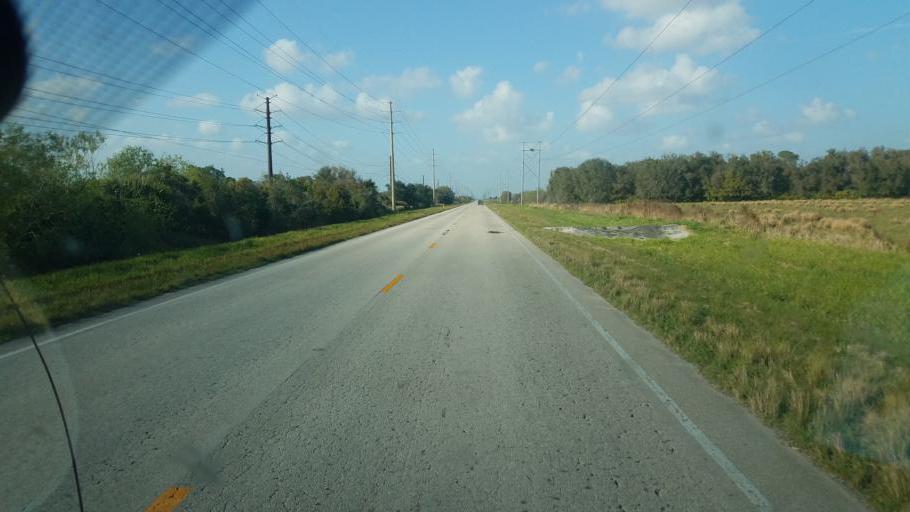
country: US
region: Florida
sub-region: Hardee County
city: Wauchula
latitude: 27.5401
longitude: -81.9297
